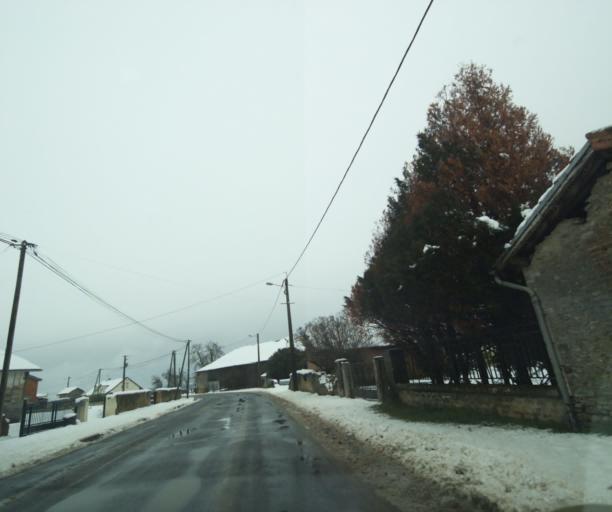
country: FR
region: Champagne-Ardenne
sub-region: Departement de la Haute-Marne
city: Montier-en-Der
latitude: 48.4412
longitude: 4.8032
